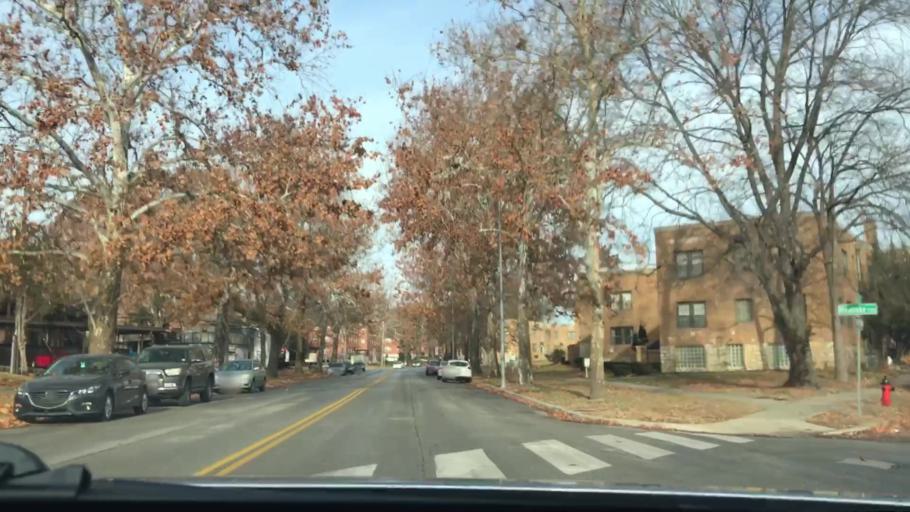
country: US
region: Kansas
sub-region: Johnson County
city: Westwood
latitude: 39.0451
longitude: -94.5997
